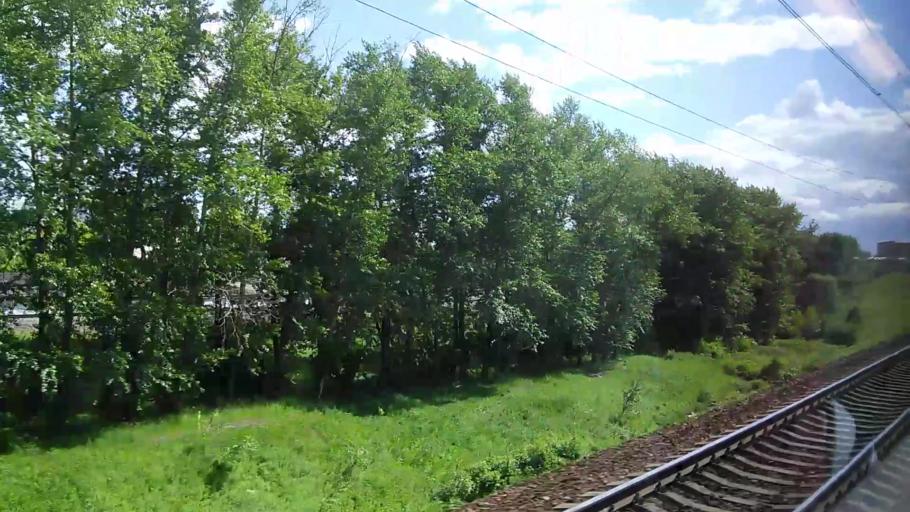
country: RU
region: Moscow
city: Likhobory
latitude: 55.8567
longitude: 37.5735
